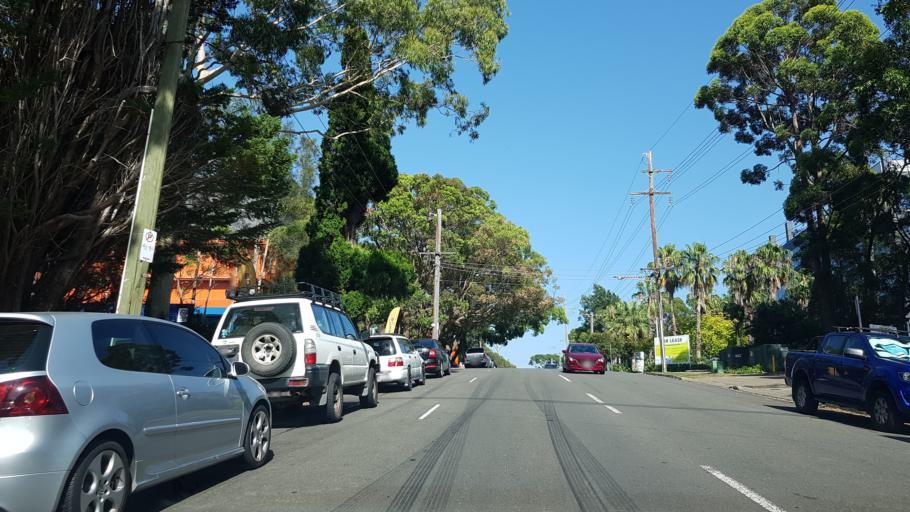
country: AU
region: New South Wales
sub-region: Warringah
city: Allambie Heights
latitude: -33.7541
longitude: 151.2471
